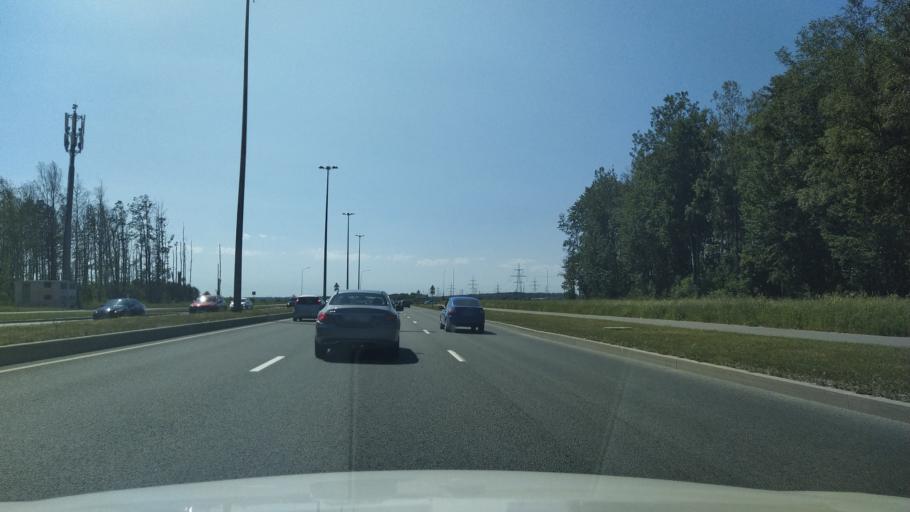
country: RU
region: St.-Petersburg
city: Levashovo
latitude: 60.0634
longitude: 30.1988
